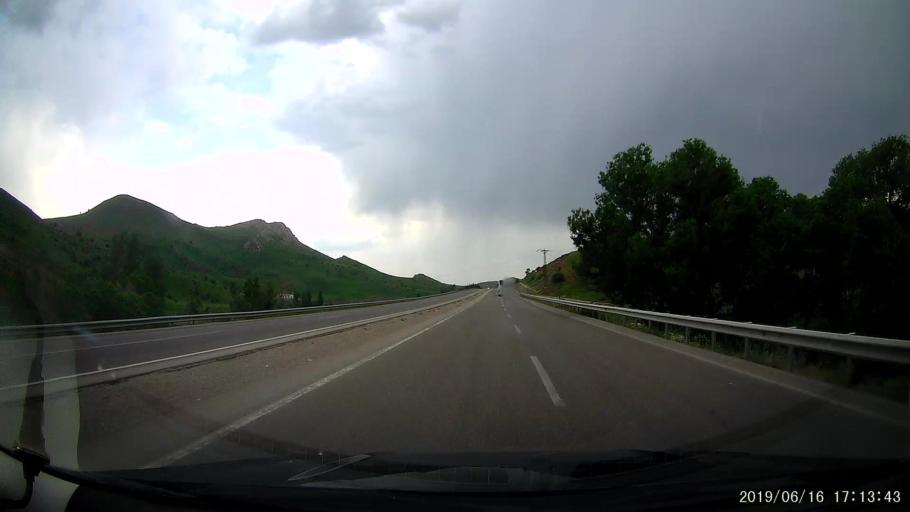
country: TR
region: Erzurum
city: Askale
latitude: 39.8573
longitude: 40.5921
